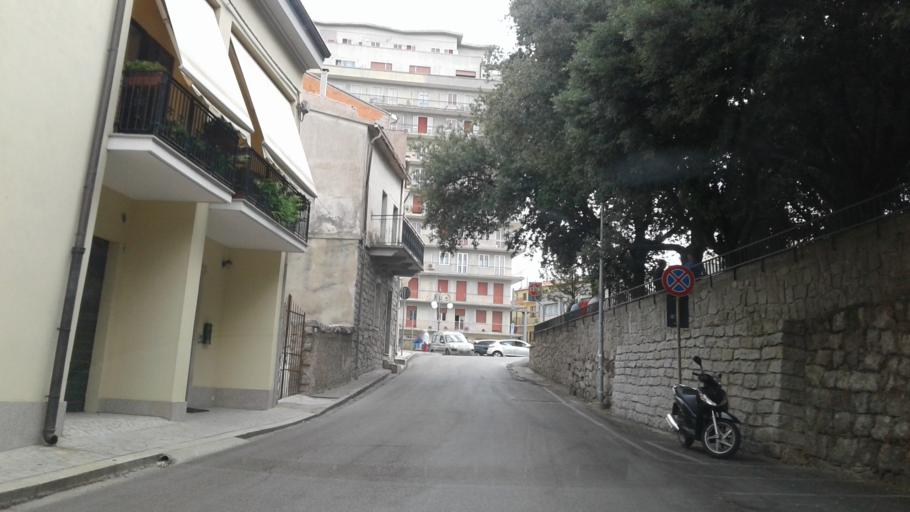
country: IT
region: Sardinia
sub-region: Provincia di Olbia-Tempio
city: Tempio Pausania
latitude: 40.9009
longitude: 9.1009
